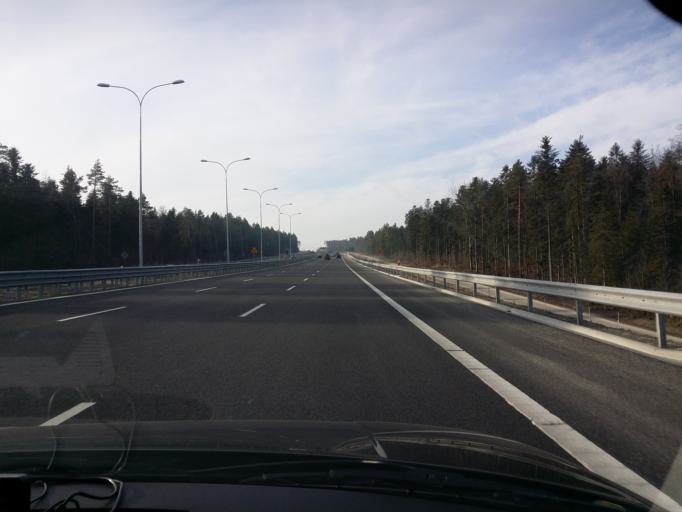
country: PL
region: Swietokrzyskie
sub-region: Powiat skarzyski
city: Skarzysko-Kamienna
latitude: 51.1541
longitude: 20.8470
